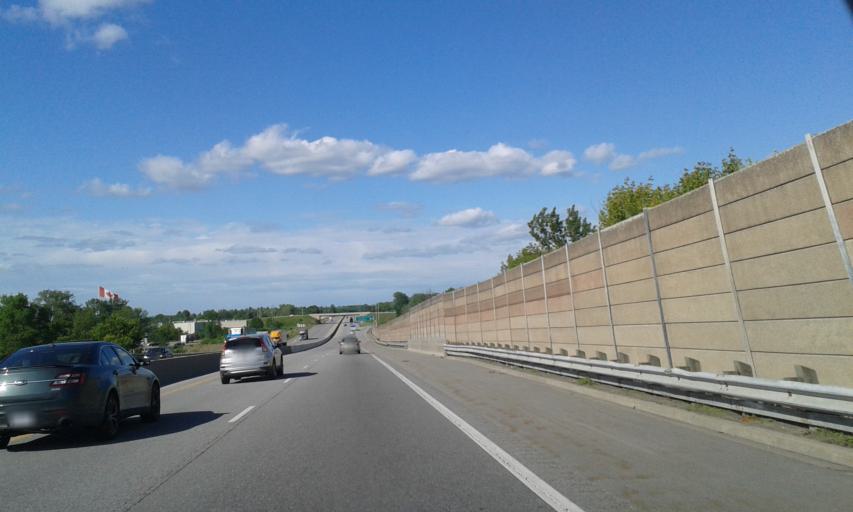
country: CA
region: Ontario
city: Brockville
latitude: 44.6061
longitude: -75.6921
